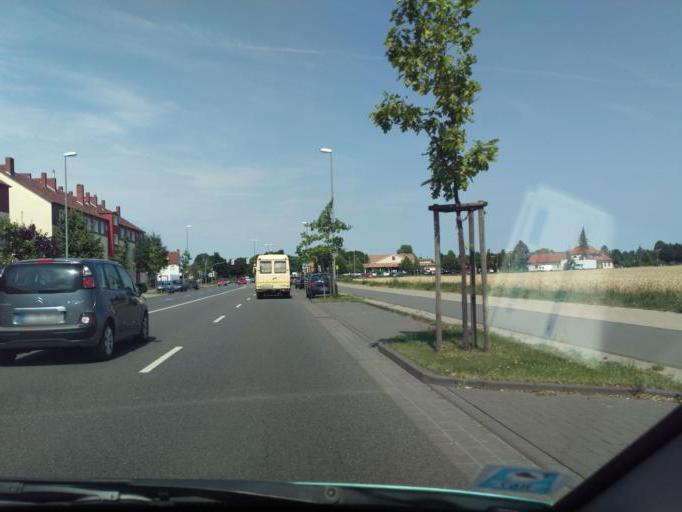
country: DE
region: Lower Saxony
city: Hildesheim
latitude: 52.1550
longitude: 9.9726
